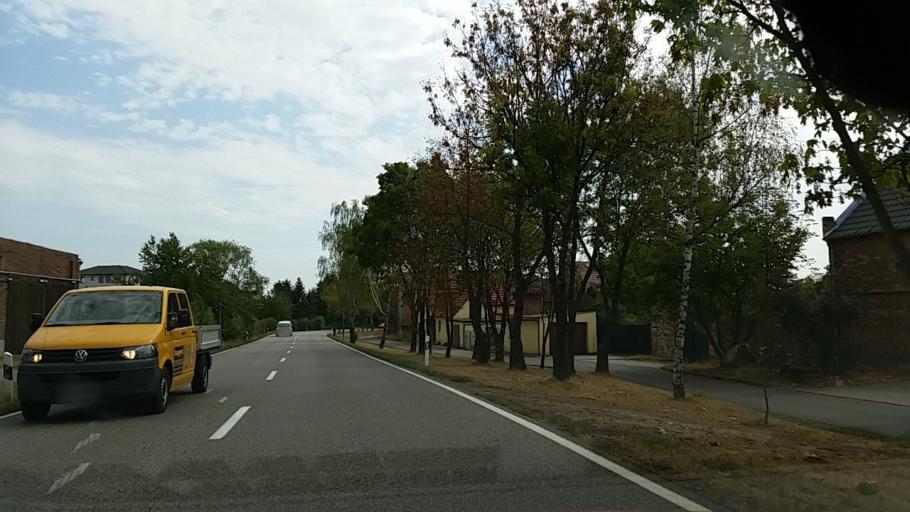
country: DE
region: Saxony-Anhalt
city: Steigra
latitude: 51.3021
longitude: 11.6587
